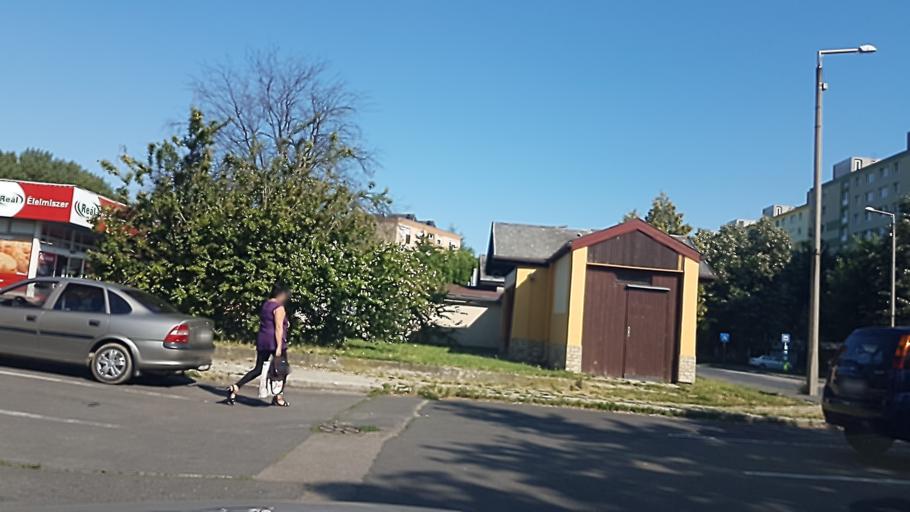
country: HU
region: Gyor-Moson-Sopron
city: Sopron
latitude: 47.6933
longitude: 16.5758
